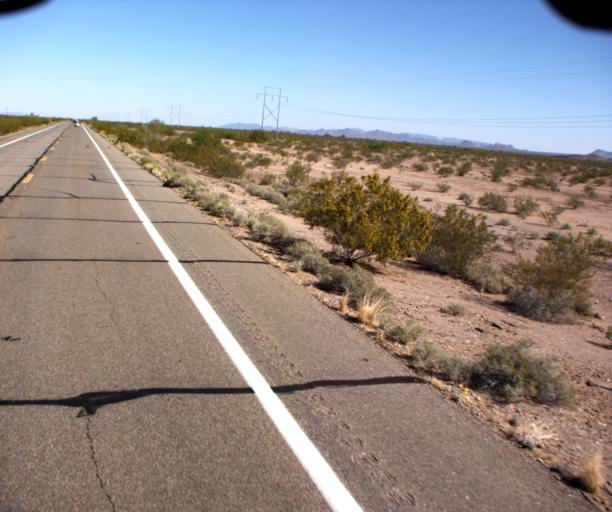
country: US
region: Arizona
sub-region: La Paz County
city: Quartzsite
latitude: 33.3235
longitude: -114.2169
